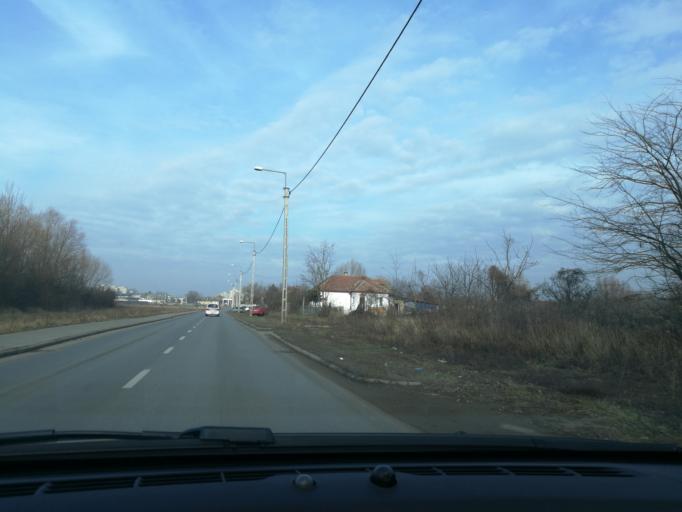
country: HU
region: Szabolcs-Szatmar-Bereg
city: Nyiregyhaza
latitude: 47.9464
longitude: 21.7396
